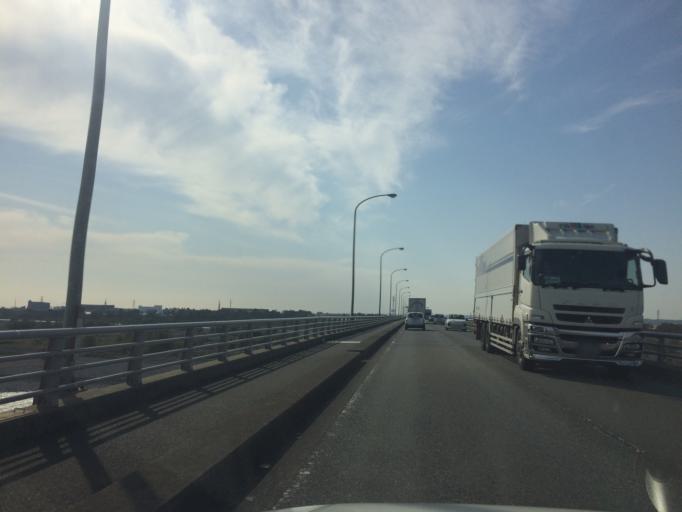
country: JP
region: Shizuoka
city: Fujieda
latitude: 34.7800
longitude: 138.2831
